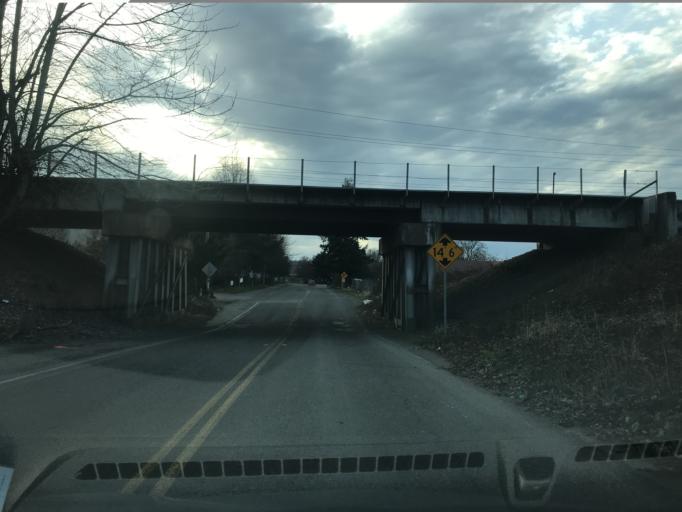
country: US
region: Washington
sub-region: King County
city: Kent
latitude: 47.3633
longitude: -122.2324
